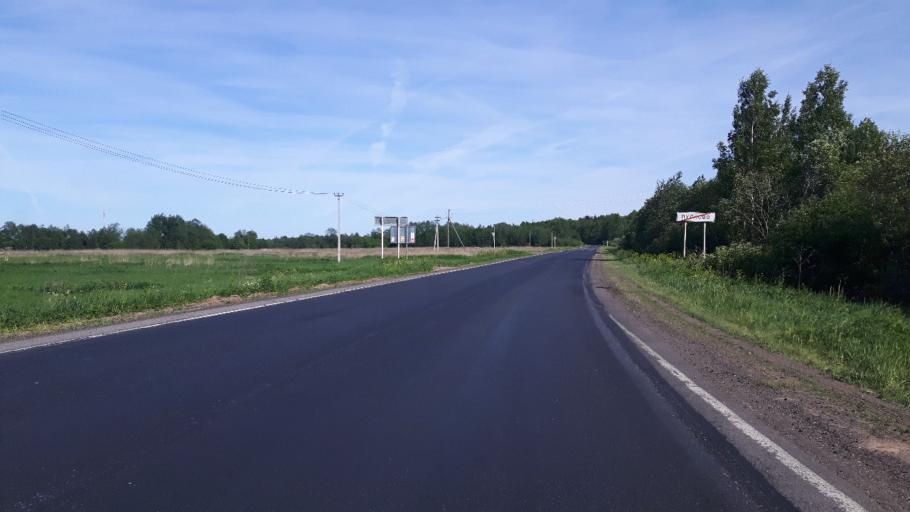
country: RU
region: Leningrad
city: Ivangorod
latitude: 59.4188
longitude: 28.3594
